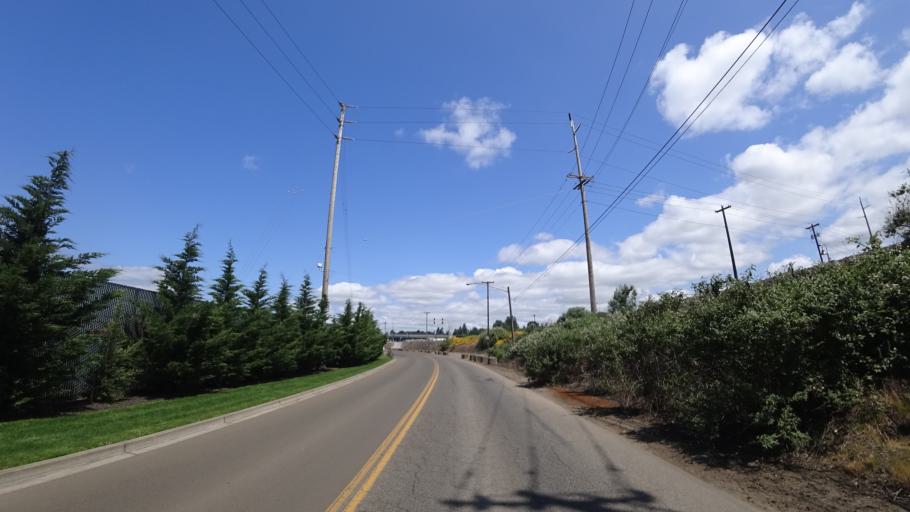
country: US
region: Washington
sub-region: Clark County
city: Vancouver
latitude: 45.6293
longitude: -122.6871
